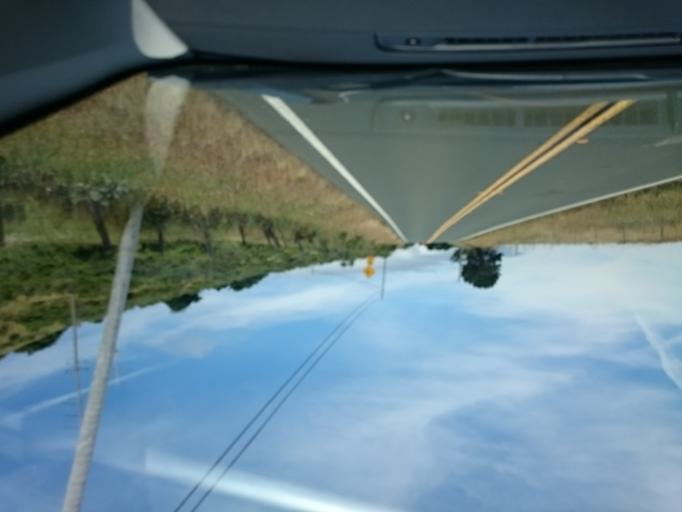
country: US
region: California
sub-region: Mendocino County
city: Boonville
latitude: 39.0977
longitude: -123.7048
